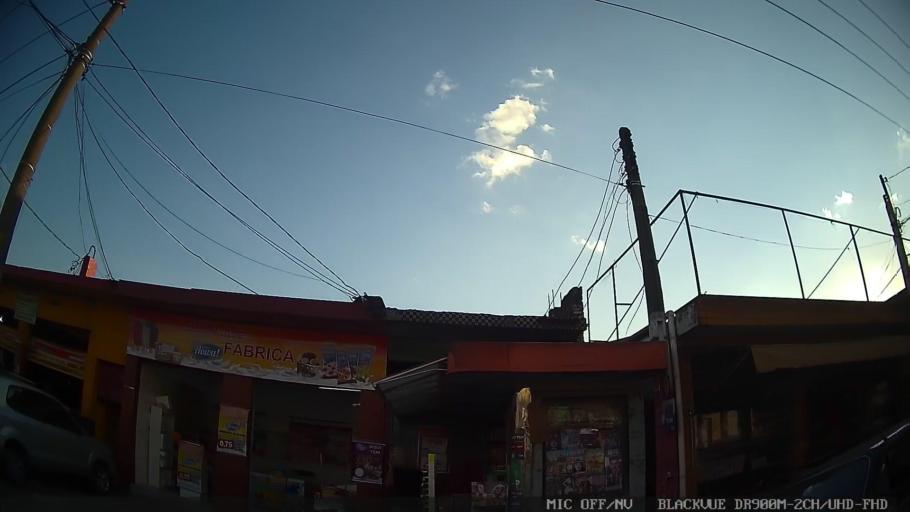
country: BR
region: Sao Paulo
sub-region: Sao Caetano Do Sul
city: Sao Caetano do Sul
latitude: -23.5839
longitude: -46.5419
